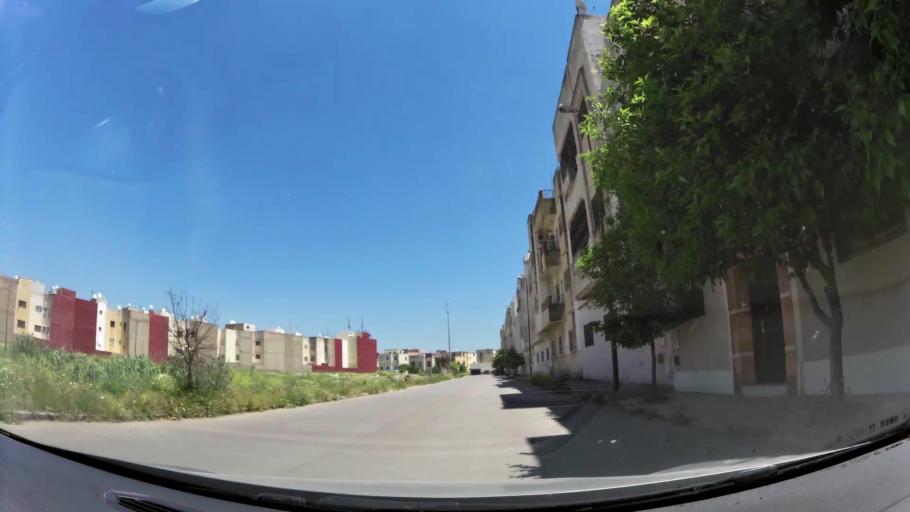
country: MA
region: Fes-Boulemane
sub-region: Fes
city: Fes
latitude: 34.0252
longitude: -5.0105
